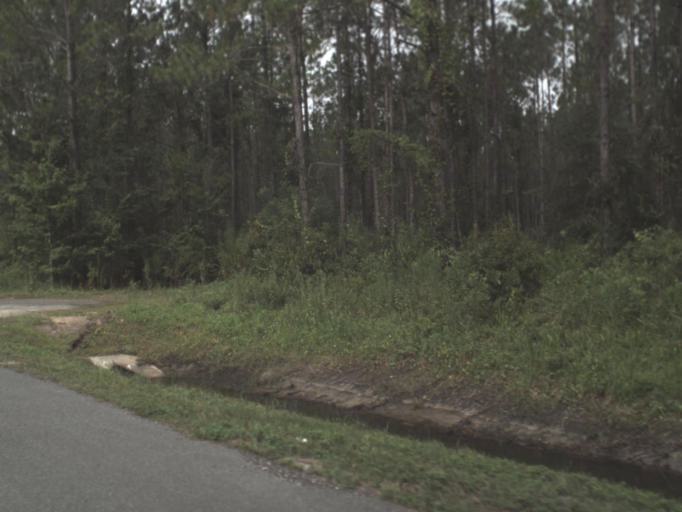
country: US
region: Florida
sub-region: Columbia County
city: Five Points
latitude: 30.2726
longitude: -82.6332
